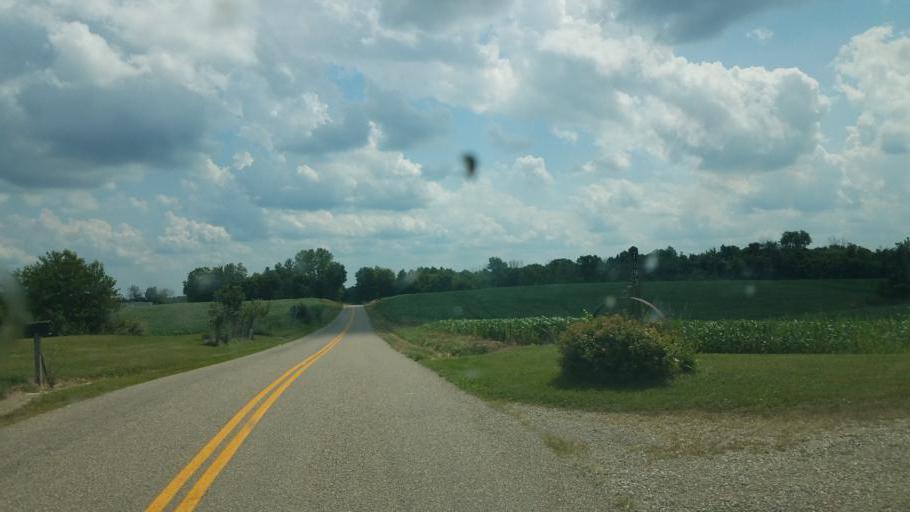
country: US
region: Ohio
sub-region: Knox County
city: Mount Vernon
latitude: 40.3552
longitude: -82.5768
